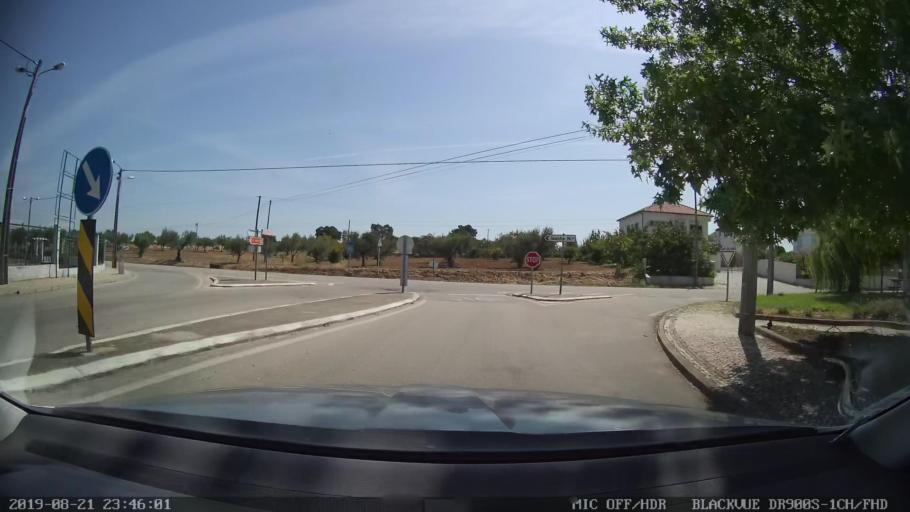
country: PT
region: Castelo Branco
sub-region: Idanha-A-Nova
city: Idanha-a-Nova
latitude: 39.8395
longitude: -7.2597
